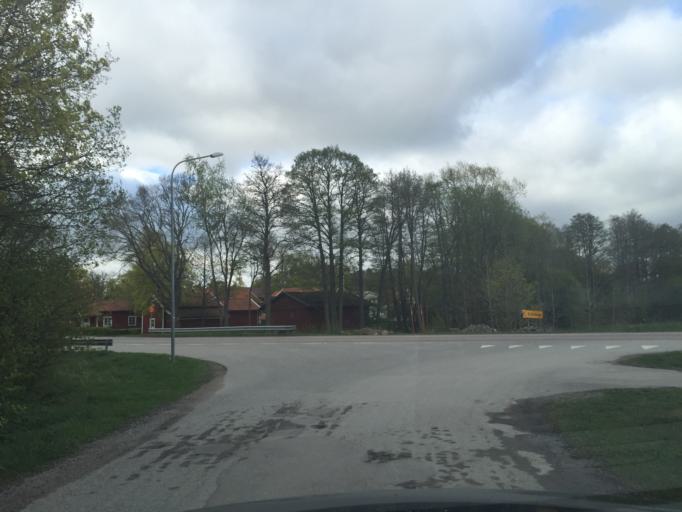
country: SE
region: Vaestmanland
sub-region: Vasteras
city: Tillberga
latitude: 59.5996
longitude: 16.7034
